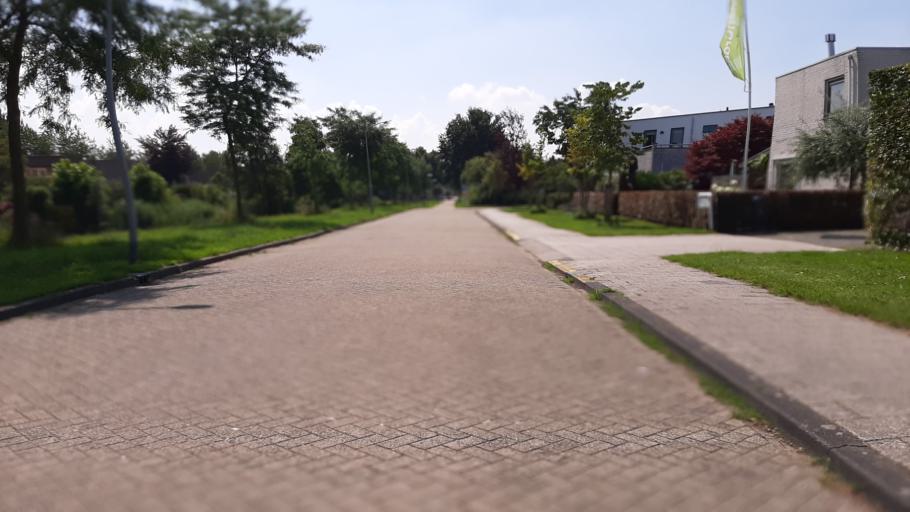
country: NL
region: Flevoland
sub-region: Gemeente Zeewolde
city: Zeewolde
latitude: 52.3247
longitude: 5.5334
